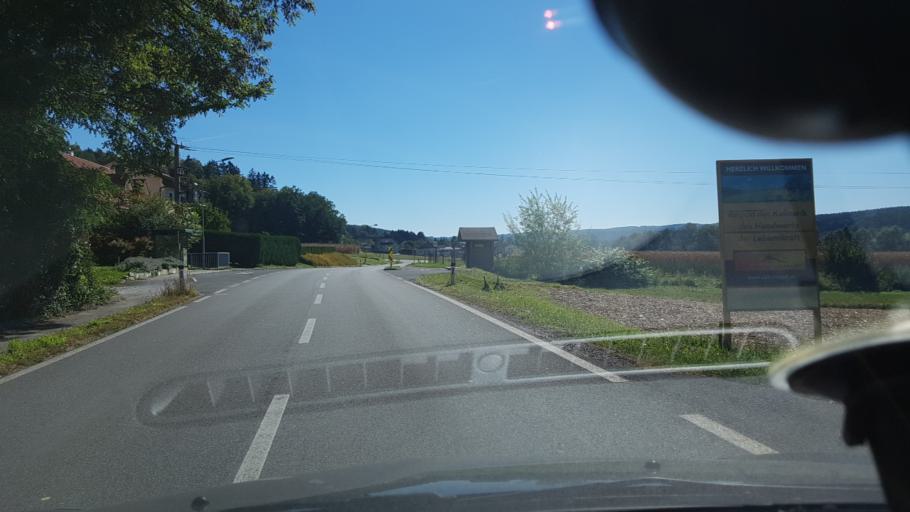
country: AT
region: Styria
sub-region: Politischer Bezirk Weiz
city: Oberrettenbach
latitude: 47.1299
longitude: 15.8060
